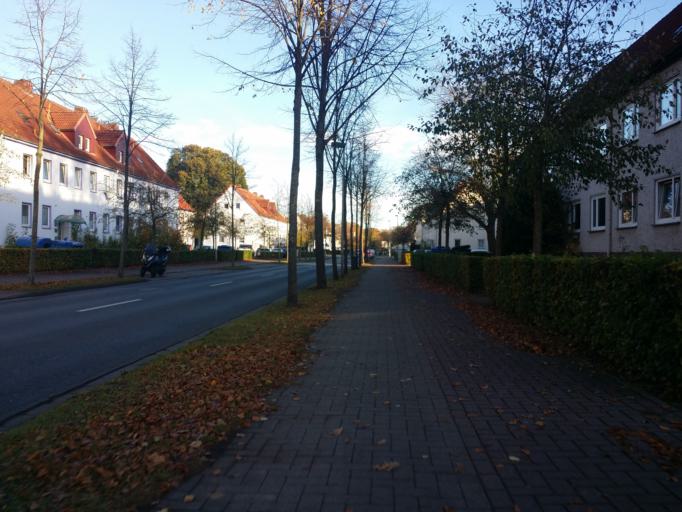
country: DE
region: Lower Saxony
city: Delmenhorst
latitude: 53.0346
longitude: 8.6400
